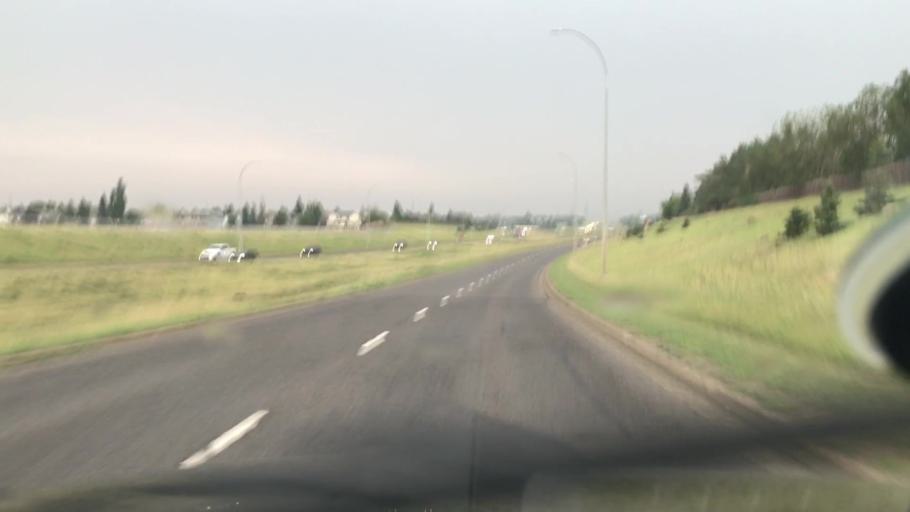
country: CA
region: Alberta
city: Edmonton
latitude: 53.4751
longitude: -113.5766
